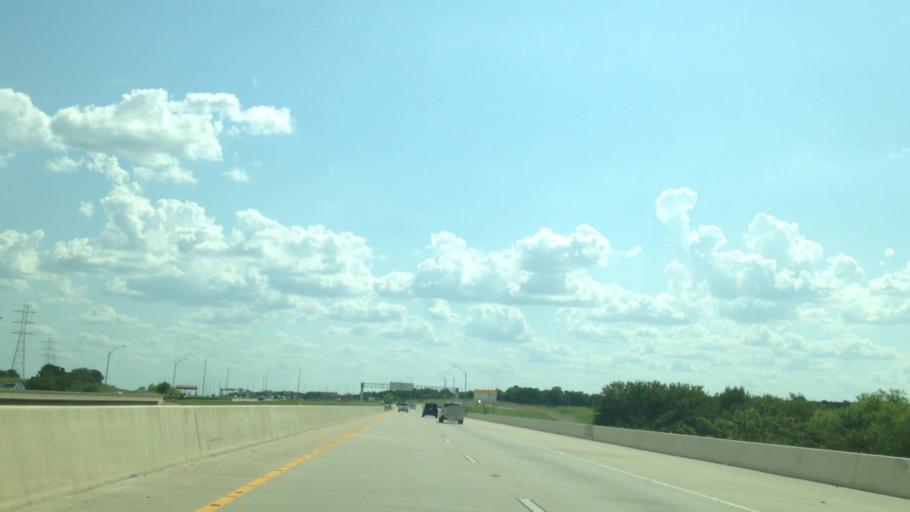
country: US
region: Texas
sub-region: Travis County
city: Hornsby Bend
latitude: 30.2762
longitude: -97.5884
